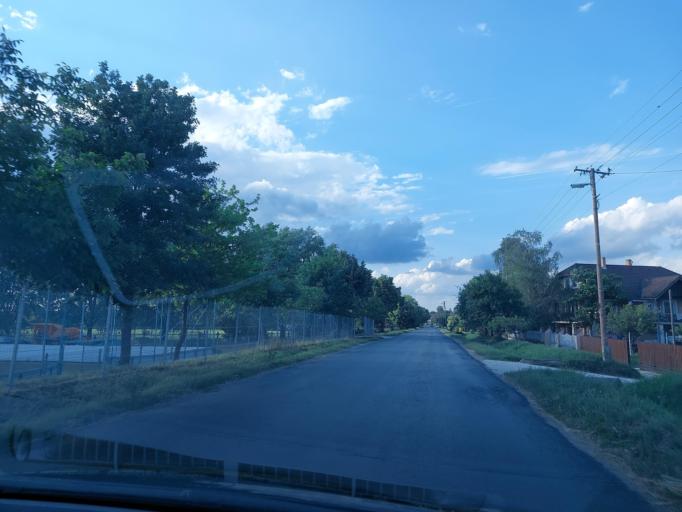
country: HU
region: Veszprem
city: Devecser
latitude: 47.1621
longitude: 17.3623
